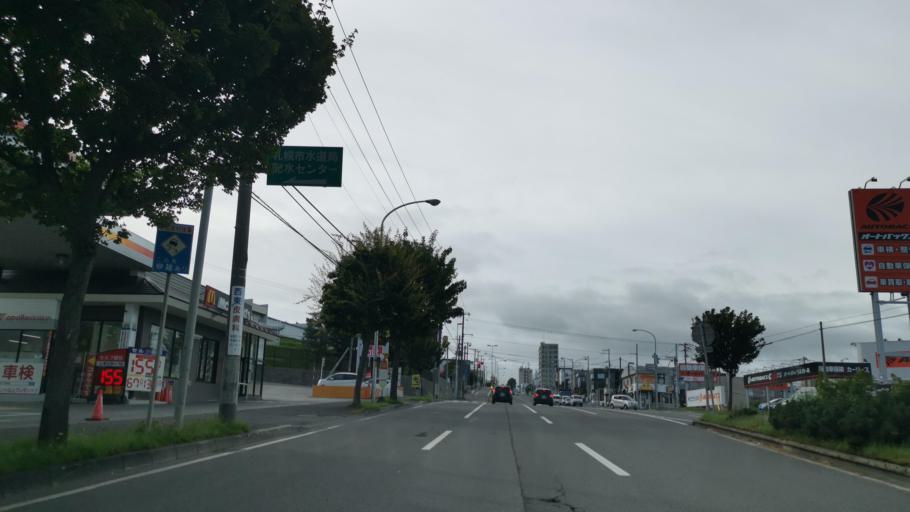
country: JP
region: Hokkaido
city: Sapporo
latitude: 43.0216
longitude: 141.3832
